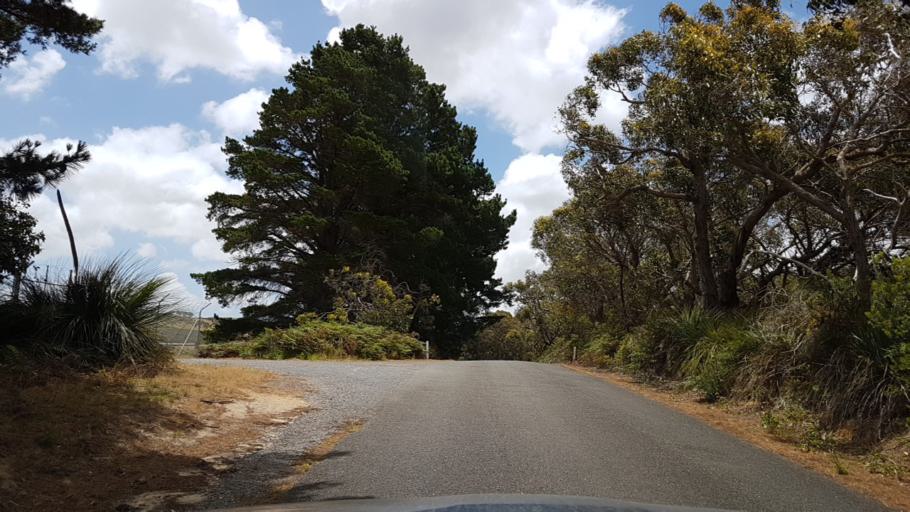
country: AU
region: South Australia
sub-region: Victor Harbor
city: Victor Harbor
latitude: -35.4538
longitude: 138.5935
